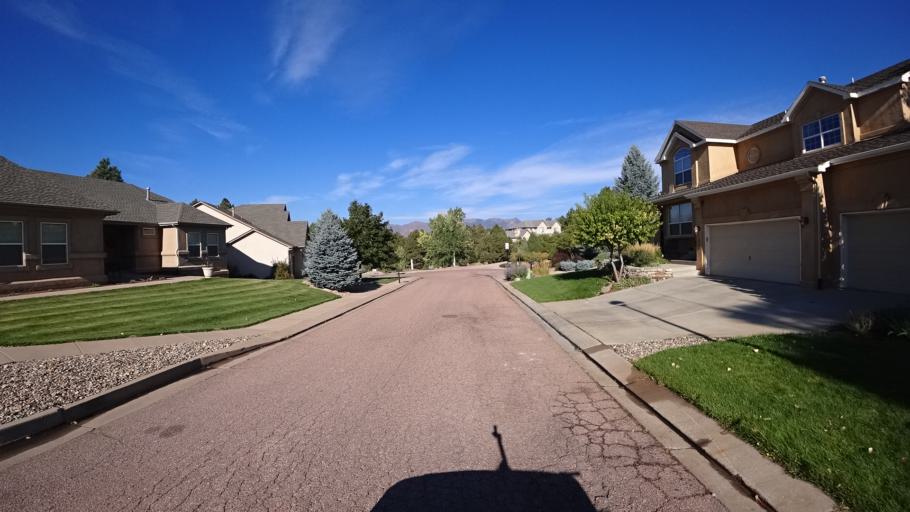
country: US
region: Colorado
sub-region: El Paso County
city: Colorado Springs
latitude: 38.9062
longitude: -104.7913
